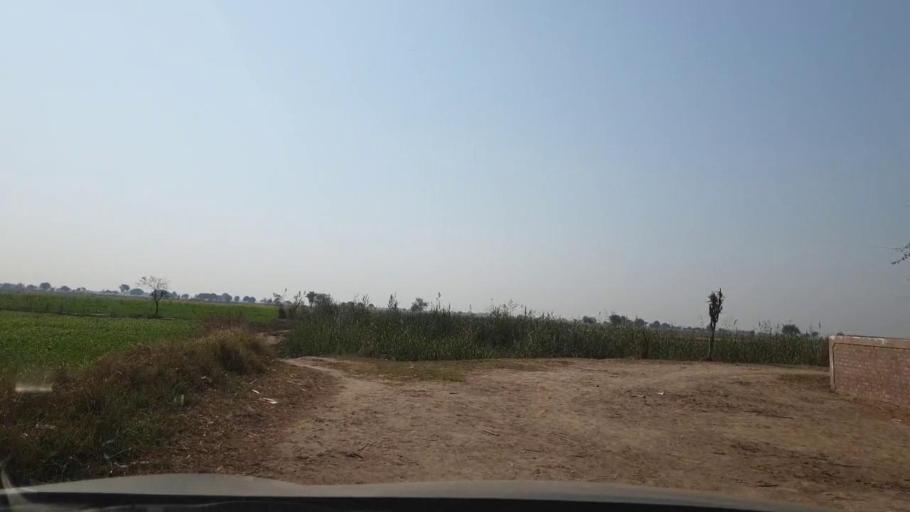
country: PK
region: Sindh
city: Berani
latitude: 25.6436
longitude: 68.8929
